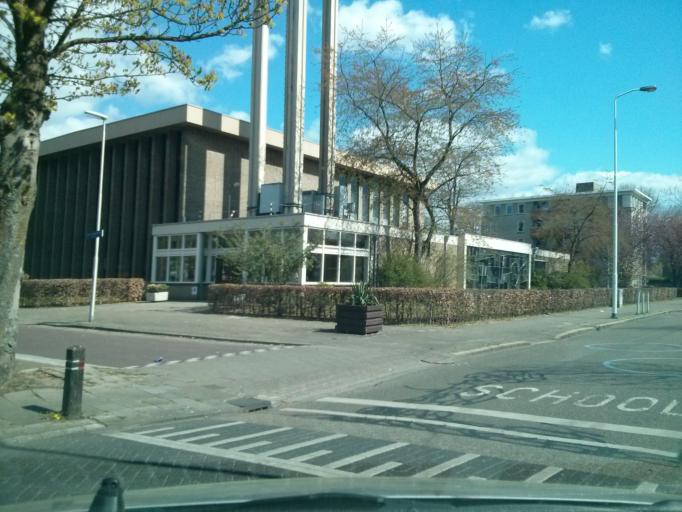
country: NL
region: North Brabant
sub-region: Gemeente Eindhoven
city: Eindhoven
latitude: 51.4620
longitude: 5.4676
